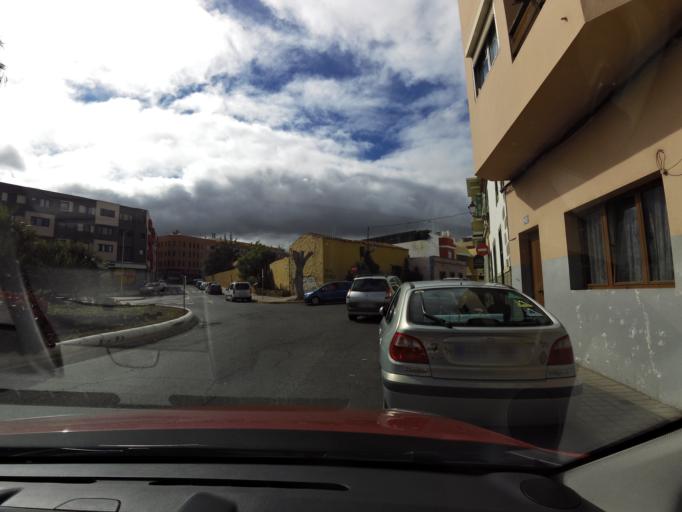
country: ES
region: Canary Islands
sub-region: Provincia de Las Palmas
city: Telde
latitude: 28.0012
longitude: -15.4172
